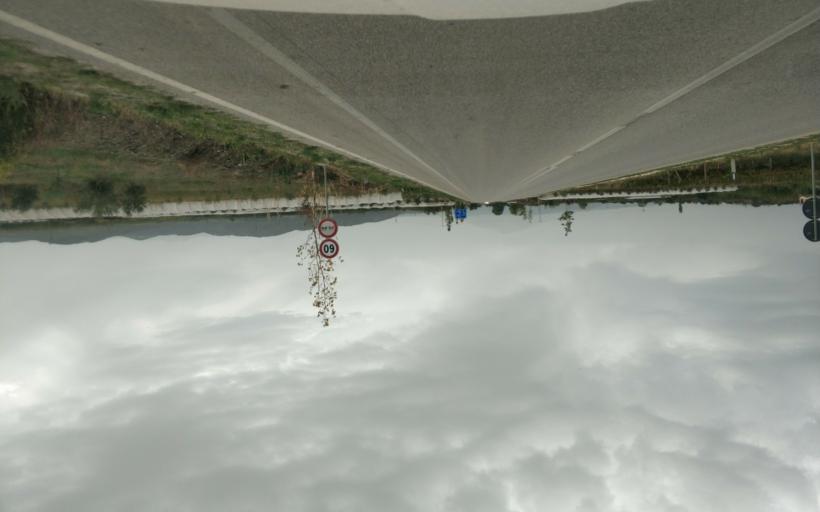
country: AL
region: Fier
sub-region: Rrethi i Fierit
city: Frakulla e Madhe
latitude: 40.6332
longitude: 19.5068
